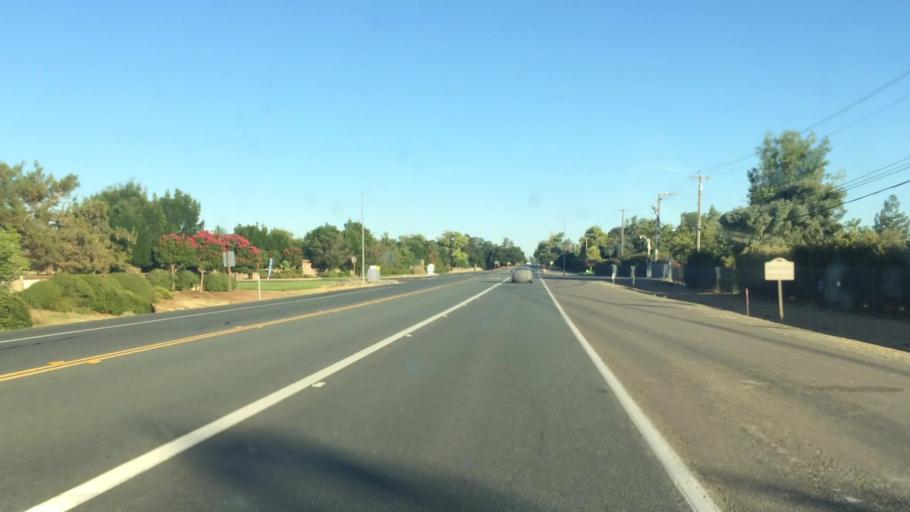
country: US
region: California
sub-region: Amador County
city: Ione
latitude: 38.3646
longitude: -120.9476
